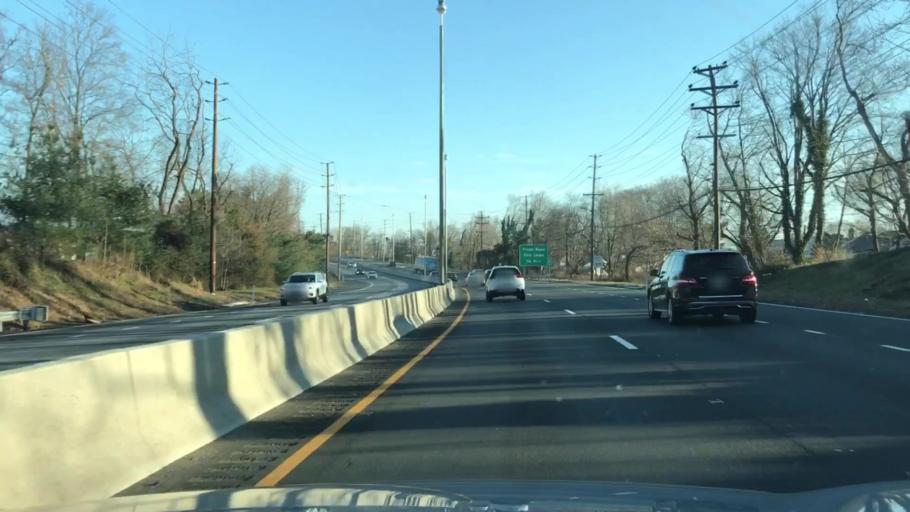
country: US
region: New Jersey
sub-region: Bergen County
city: Fair Lawn
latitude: 40.9360
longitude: -74.1241
